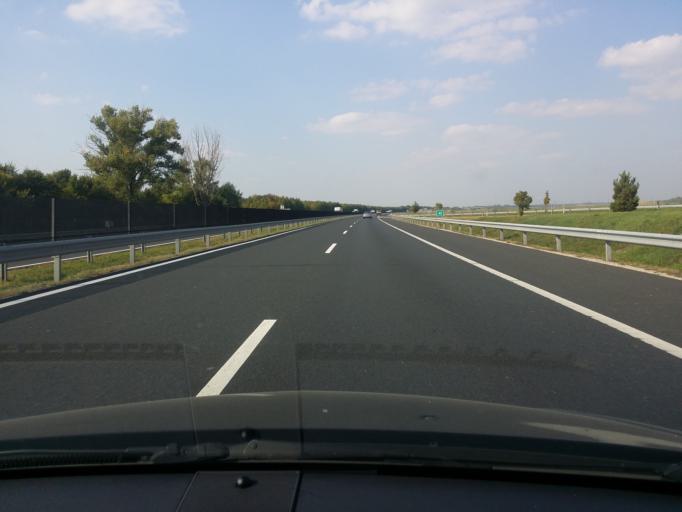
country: HU
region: Fejer
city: Ivancsa
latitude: 47.1312
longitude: 18.8180
